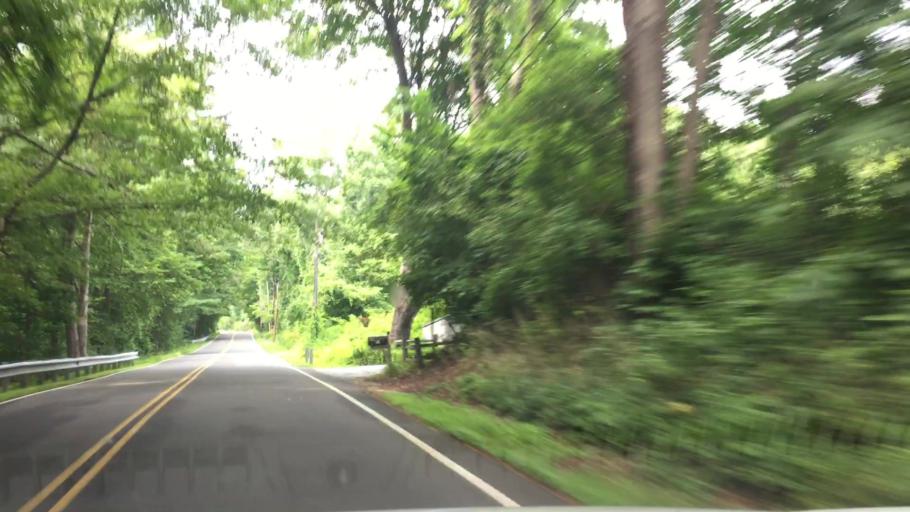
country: US
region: Massachusetts
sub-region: Berkshire County
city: Housatonic
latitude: 42.2228
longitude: -73.4054
